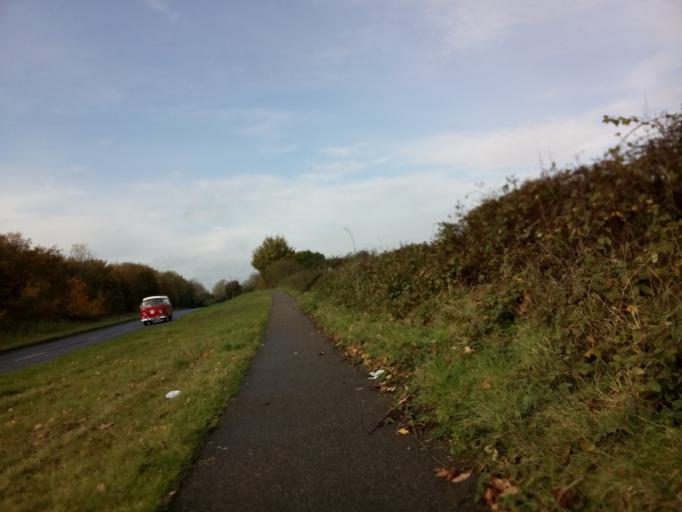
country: GB
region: England
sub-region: Suffolk
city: Needham Market
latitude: 52.1662
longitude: 1.0327
